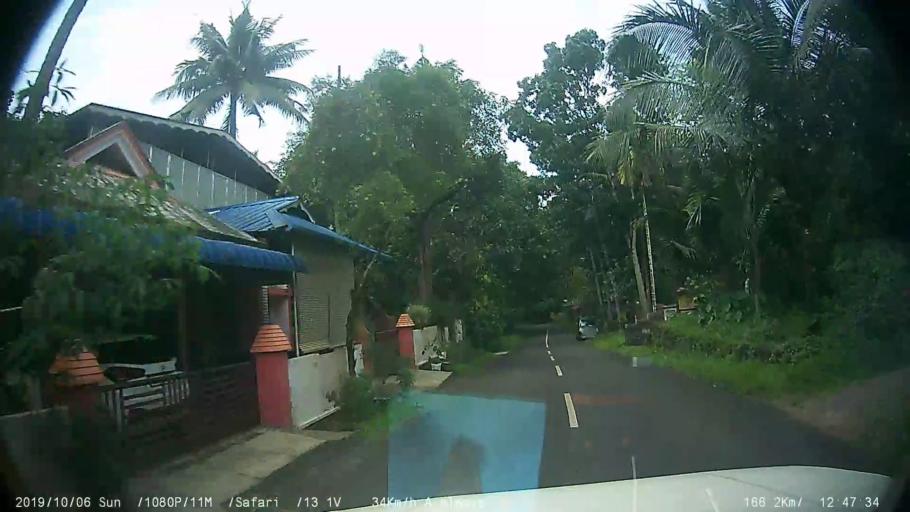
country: IN
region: Kerala
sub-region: Kottayam
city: Palackattumala
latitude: 9.7754
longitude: 76.6012
